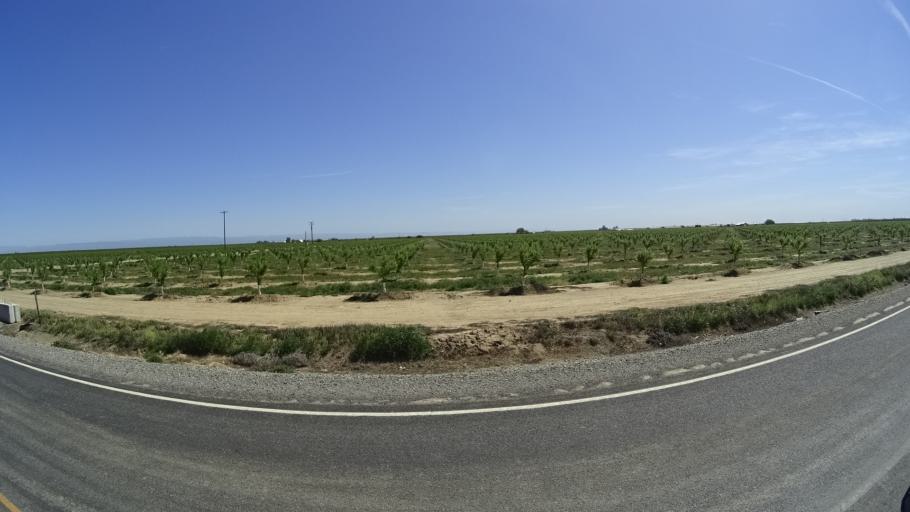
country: US
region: California
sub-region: Glenn County
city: Orland
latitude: 39.6485
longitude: -122.1409
